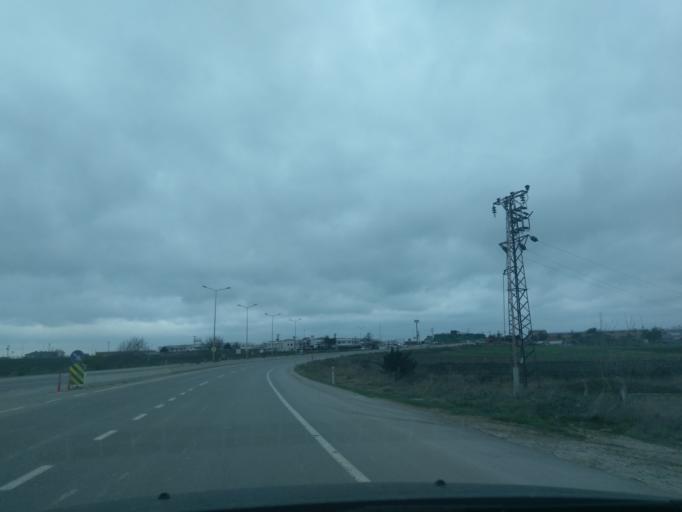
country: TR
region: Istanbul
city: Muratbey
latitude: 41.1228
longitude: 28.4906
